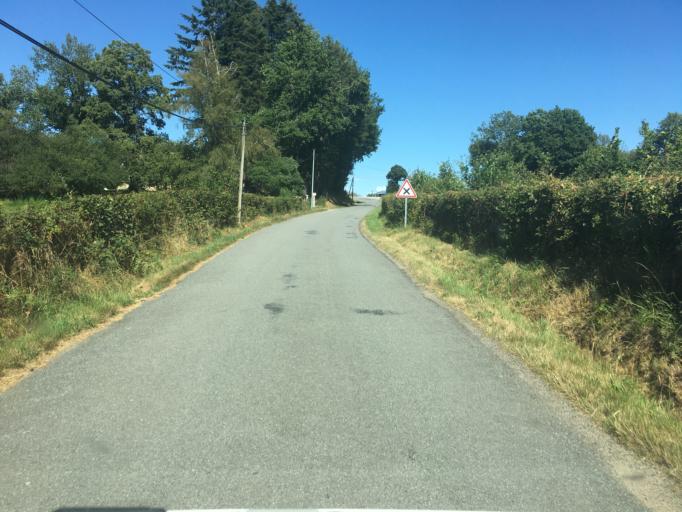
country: FR
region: Limousin
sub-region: Departement de la Correze
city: Bort-les-Orgues
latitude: 45.4431
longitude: 2.4802
